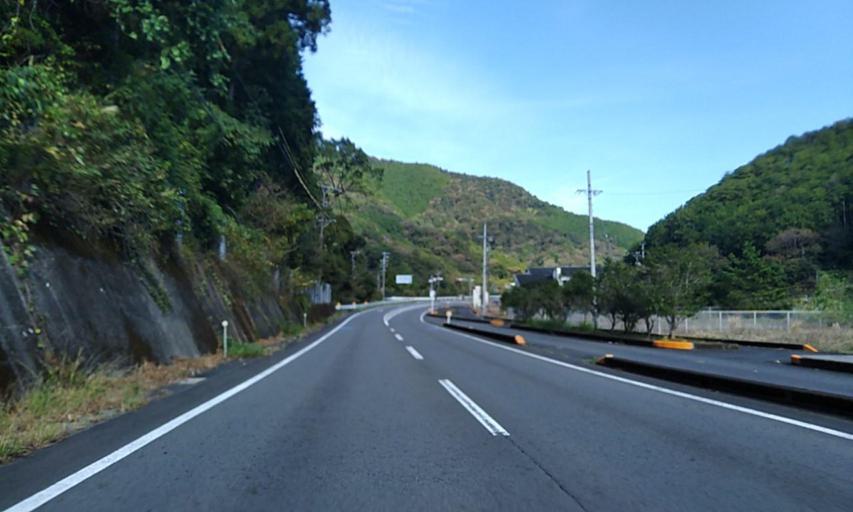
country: JP
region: Mie
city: Owase
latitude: 34.1945
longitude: 136.3149
